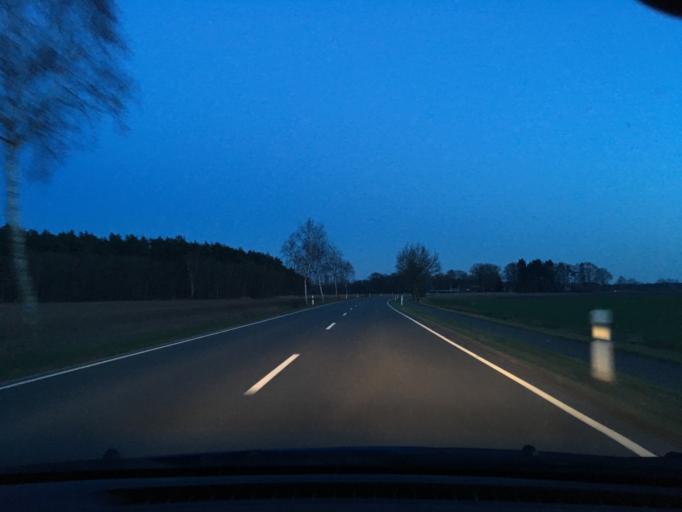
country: DE
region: Lower Saxony
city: Oldendorf
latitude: 53.1839
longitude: 10.2086
